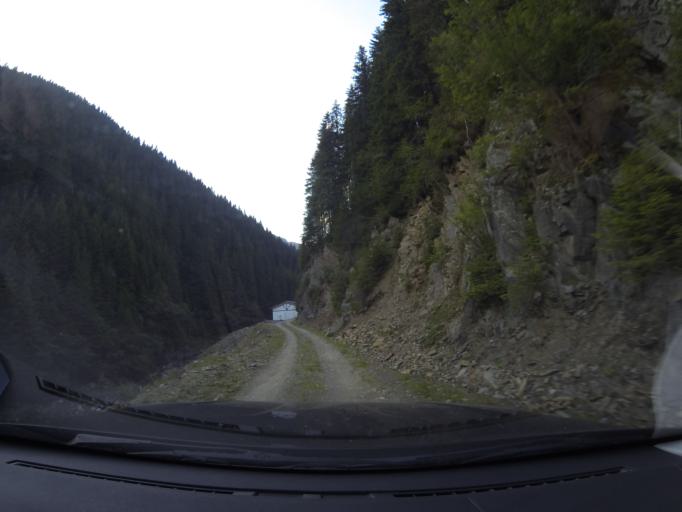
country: RO
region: Brasov
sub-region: Oras Victoria
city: Victoria
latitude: 45.5547
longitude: 24.6825
